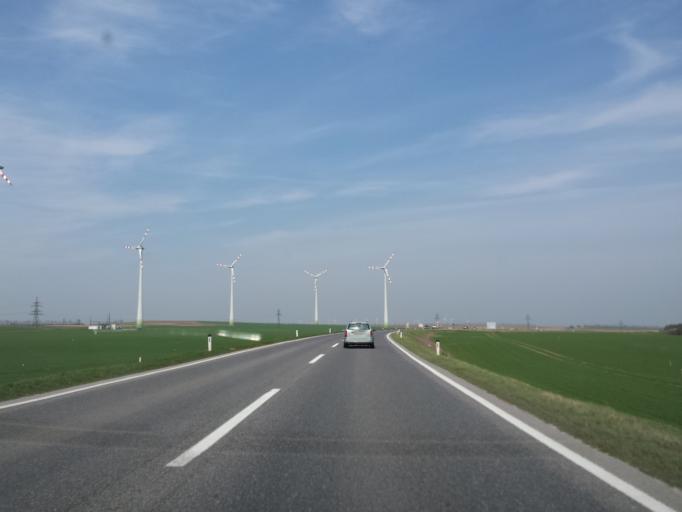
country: AT
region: Lower Austria
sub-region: Politischer Bezirk Mistelbach
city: Wilfersdorf
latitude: 48.5375
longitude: 16.6266
